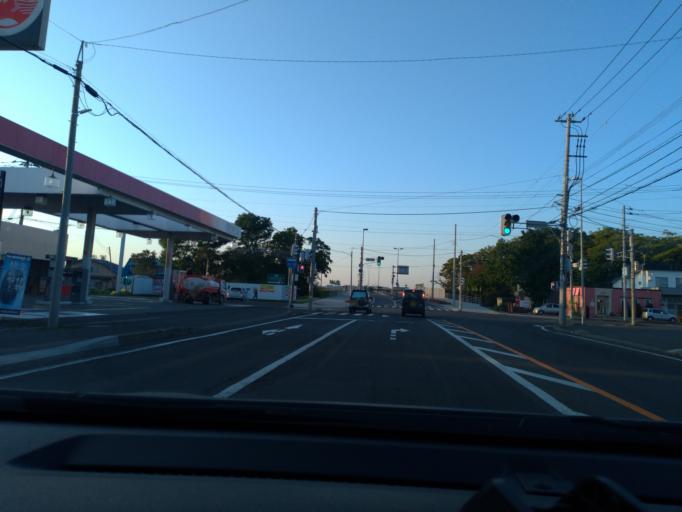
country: JP
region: Hokkaido
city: Tobetsu
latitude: 43.2117
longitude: 141.5182
